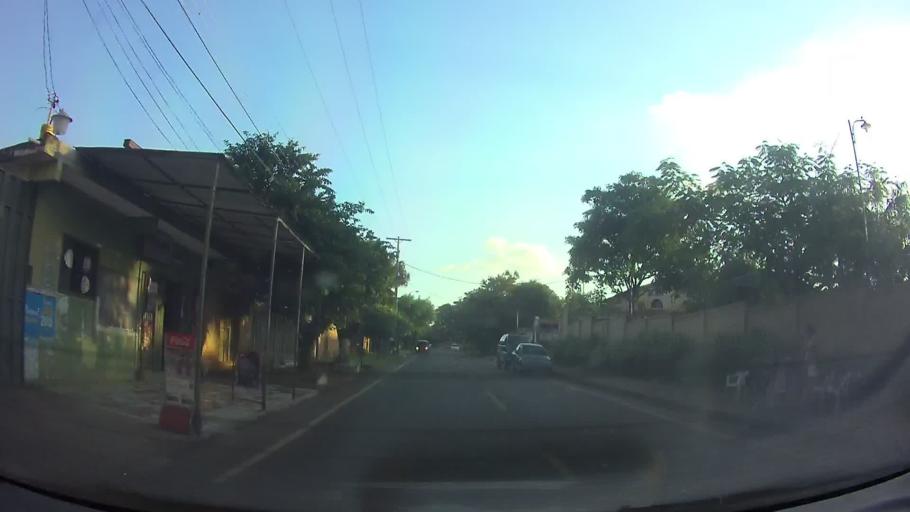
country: PY
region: Central
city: Limpio
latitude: -25.2522
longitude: -57.4985
